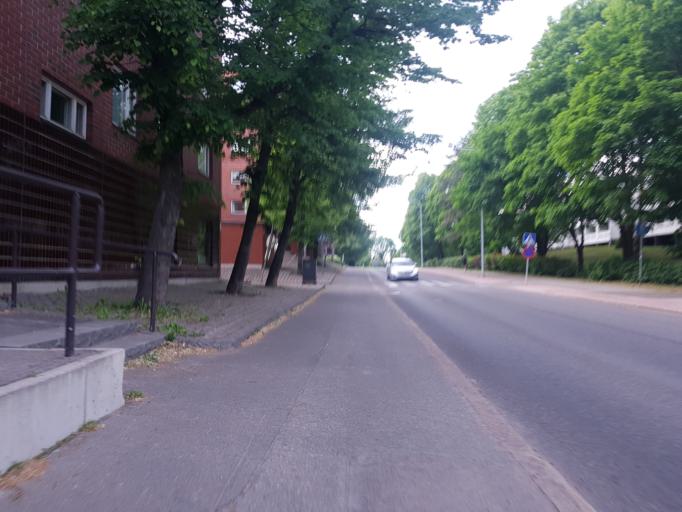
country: FI
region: Uusimaa
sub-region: Helsinki
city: Vantaa
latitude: 60.2462
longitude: 24.9924
